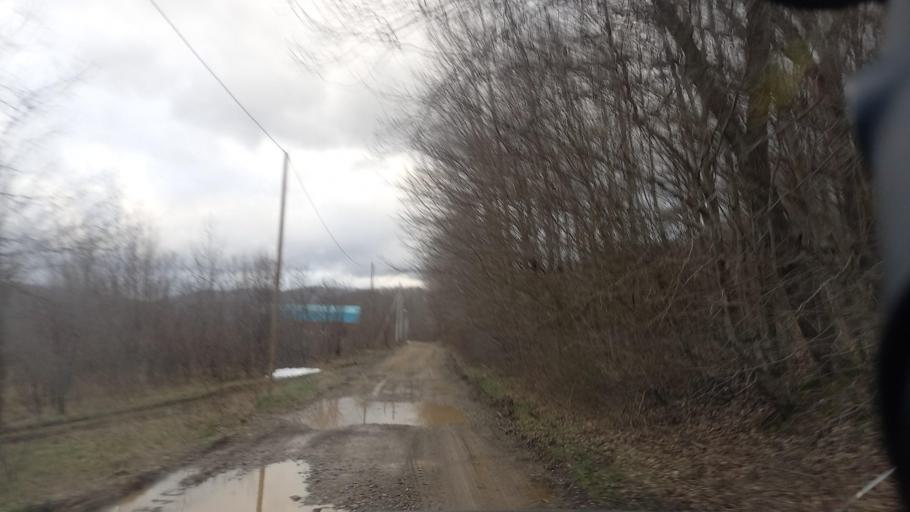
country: RU
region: Krasnodarskiy
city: Lermontovo
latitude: 44.4299
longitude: 38.8011
